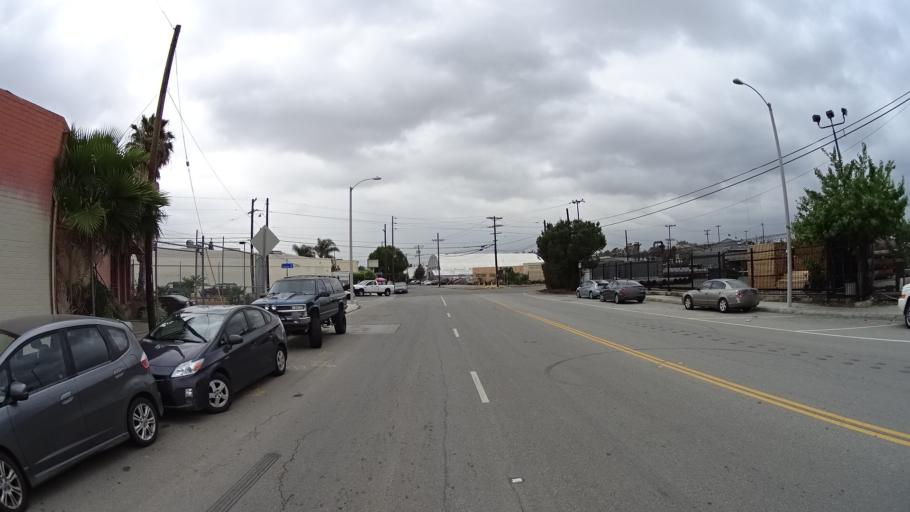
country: US
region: California
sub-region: Los Angeles County
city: Boyle Heights
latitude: 34.0615
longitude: -118.1922
